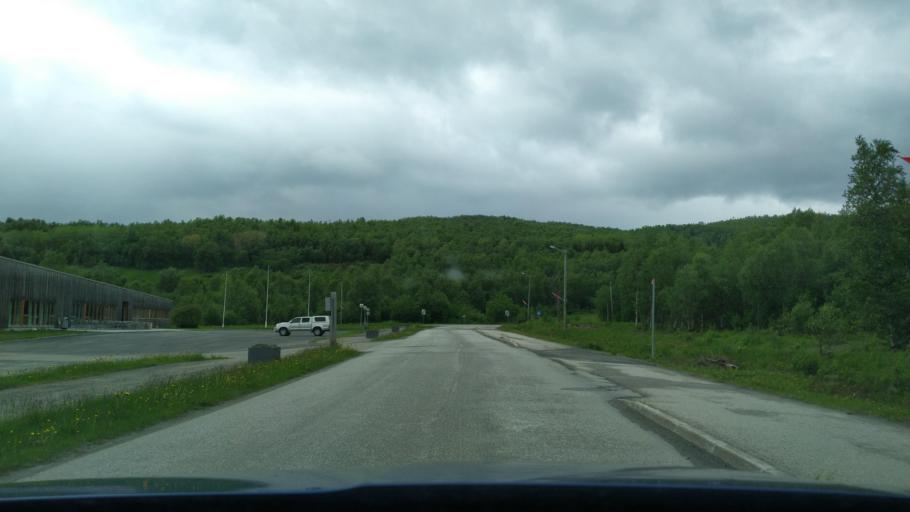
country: NO
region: Troms
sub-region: Dyroy
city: Brostadbotn
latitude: 69.0917
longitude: 17.6955
